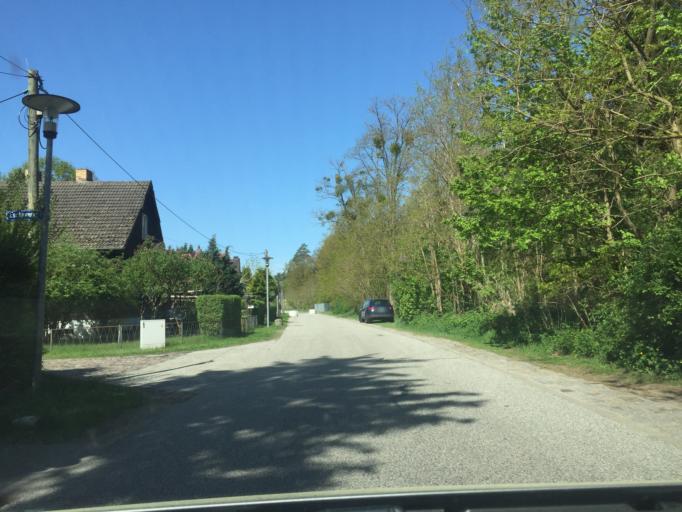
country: DE
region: Mecklenburg-Vorpommern
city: Torgelow
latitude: 53.6202
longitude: 14.0327
